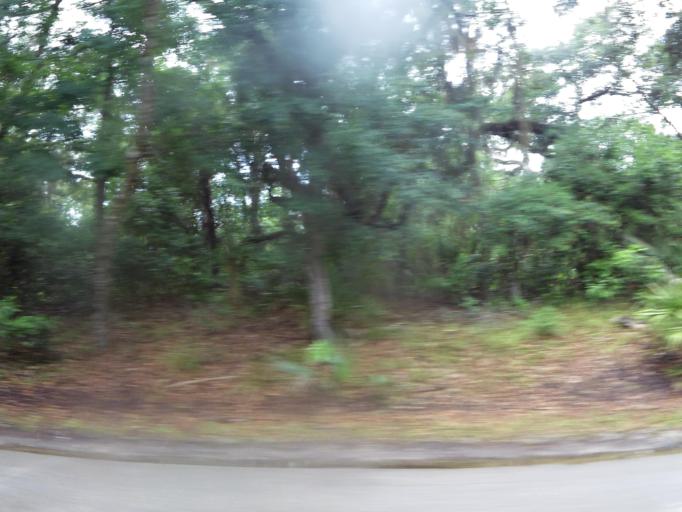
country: US
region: Florida
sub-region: Nassau County
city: Fernandina Beach
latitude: 30.6928
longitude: -81.4391
